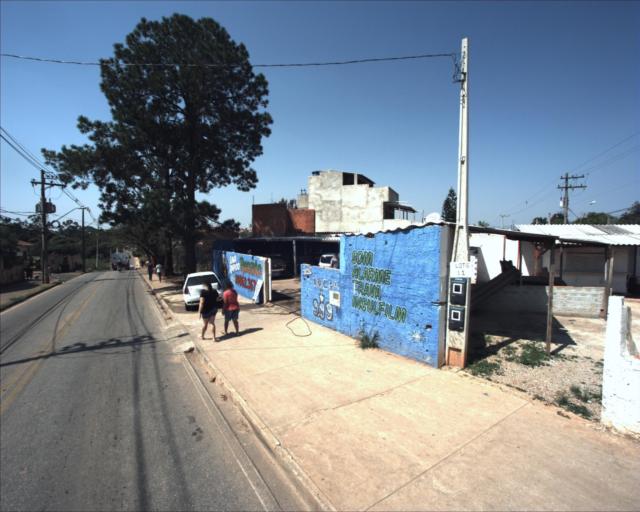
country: BR
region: Sao Paulo
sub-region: Sorocaba
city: Sorocaba
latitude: -23.4560
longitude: -47.5006
